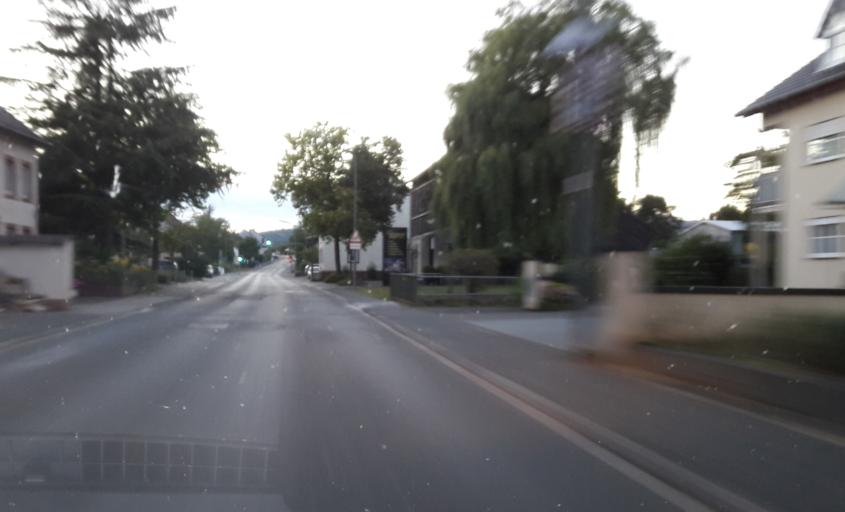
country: DE
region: Rheinland-Pfalz
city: Neuerburg
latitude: 49.9896
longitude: 6.9458
